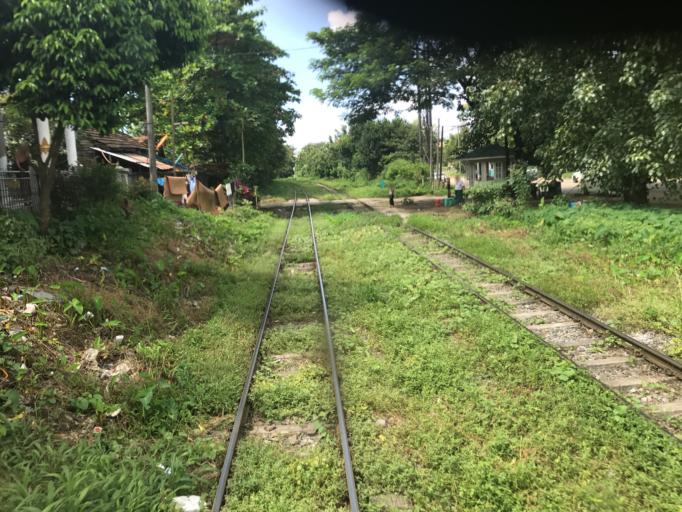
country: MM
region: Yangon
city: Yangon
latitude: 16.8901
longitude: 96.1047
